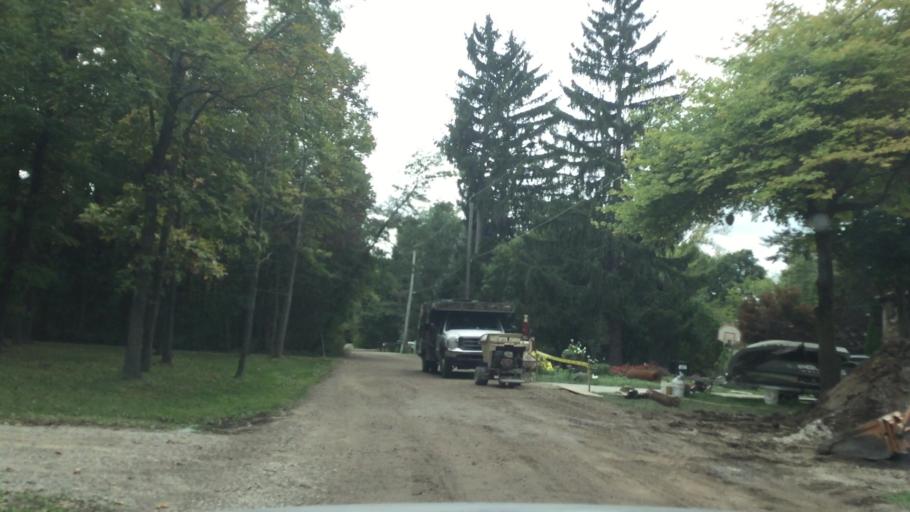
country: US
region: Michigan
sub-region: Livingston County
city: Brighton
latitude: 42.5614
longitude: -83.7430
